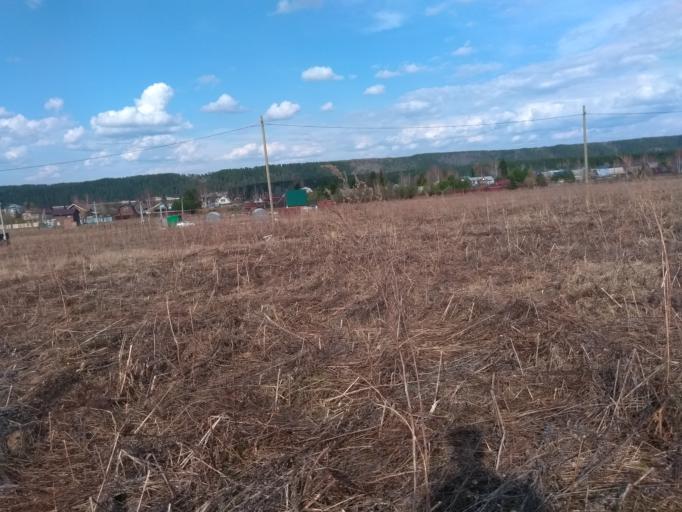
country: RU
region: Perm
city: Sylva
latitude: 57.8444
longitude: 56.7870
